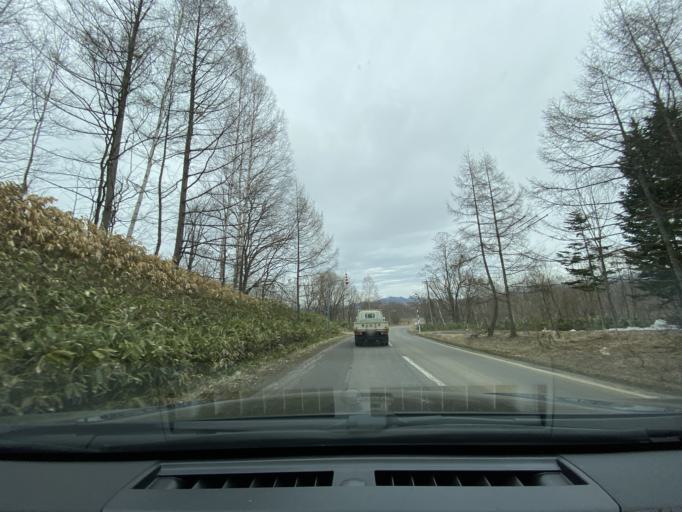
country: JP
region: Hokkaido
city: Nayoro
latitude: 44.0929
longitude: 142.4655
